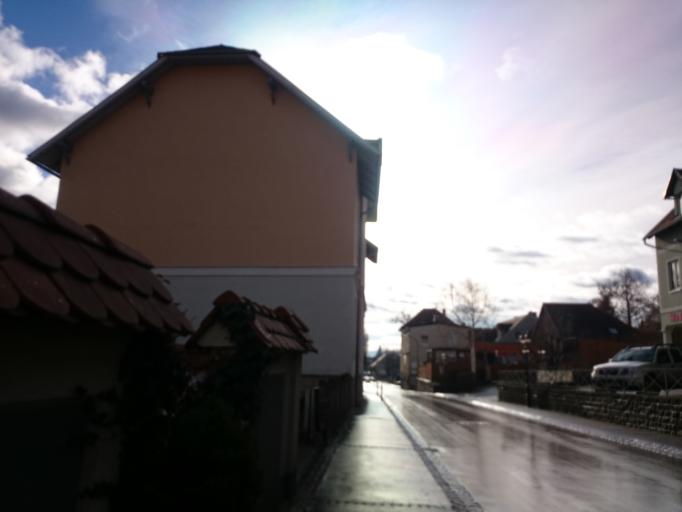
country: AT
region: Styria
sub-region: Politischer Bezirk Weiz
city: Weiz
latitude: 47.2167
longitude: 15.6229
